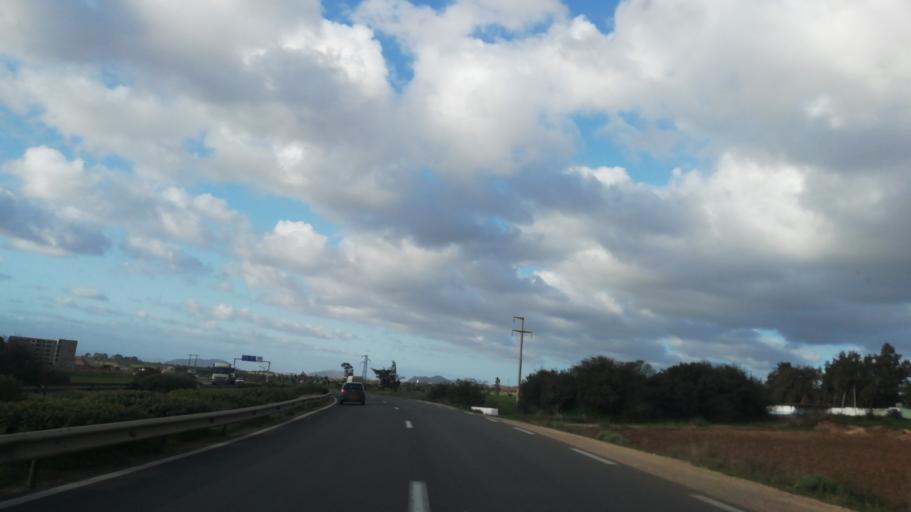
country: DZ
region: Ain Temouchent
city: El Amria
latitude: 35.4617
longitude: -1.0538
